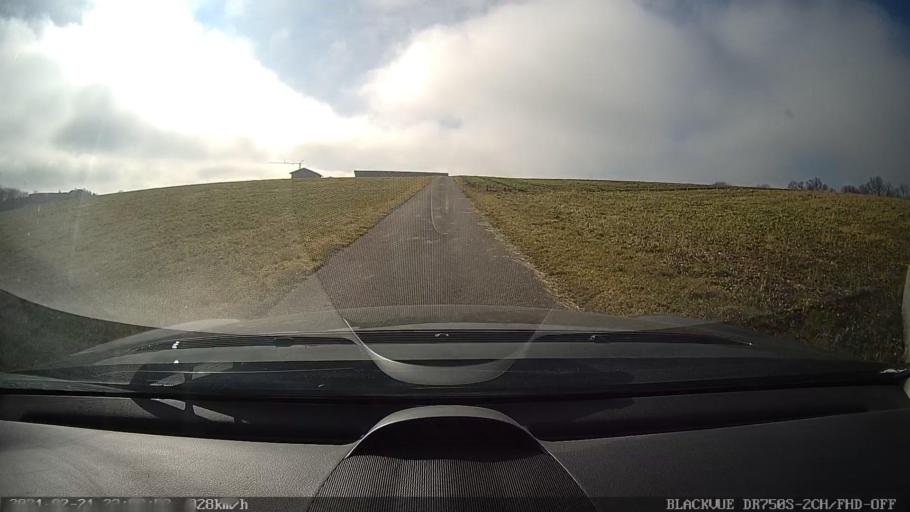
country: DE
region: Bavaria
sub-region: Upper Bavaria
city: Griesstatt
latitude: 48.0050
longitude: 12.1787
